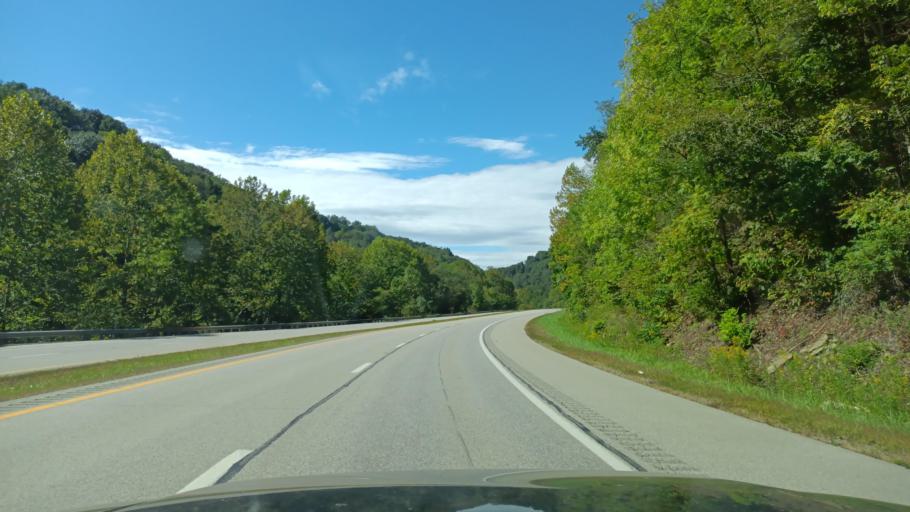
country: US
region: West Virginia
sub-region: Harrison County
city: Salem
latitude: 39.2853
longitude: -80.6483
